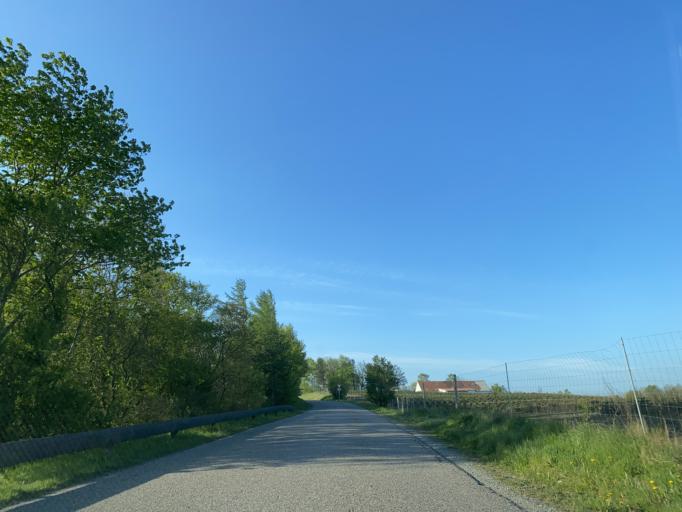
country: DK
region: Central Jutland
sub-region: Silkeborg Kommune
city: Silkeborg
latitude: 56.2109
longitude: 9.5619
